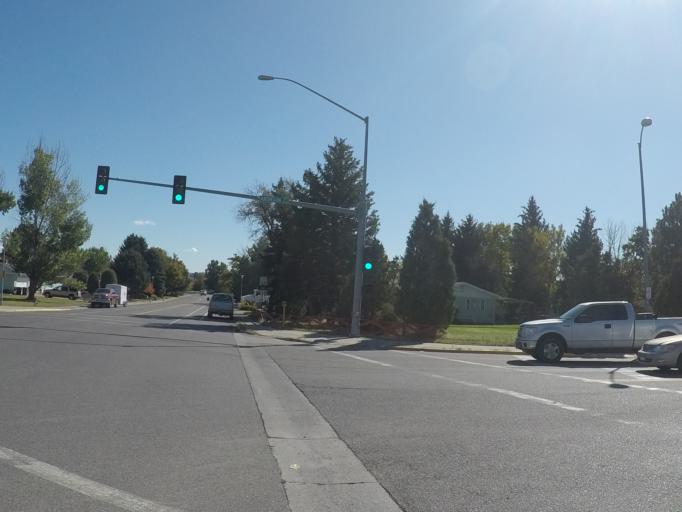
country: US
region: Montana
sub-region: Yellowstone County
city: Billings
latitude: 45.8144
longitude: -108.4955
